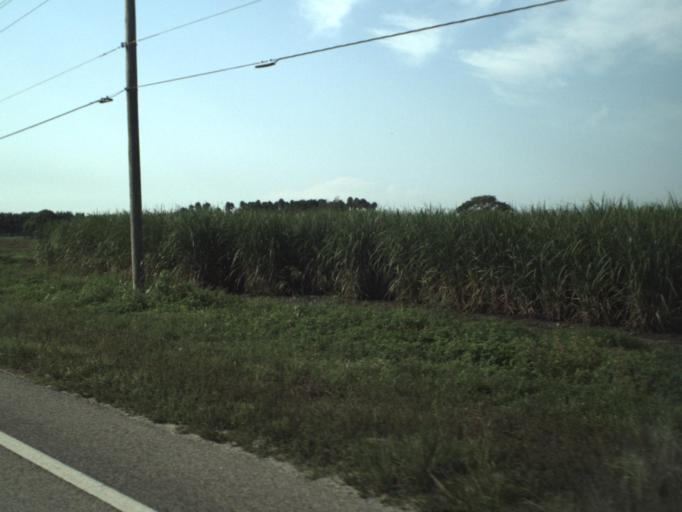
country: US
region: Florida
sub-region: Hendry County
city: Clewiston
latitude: 26.7093
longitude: -80.8336
